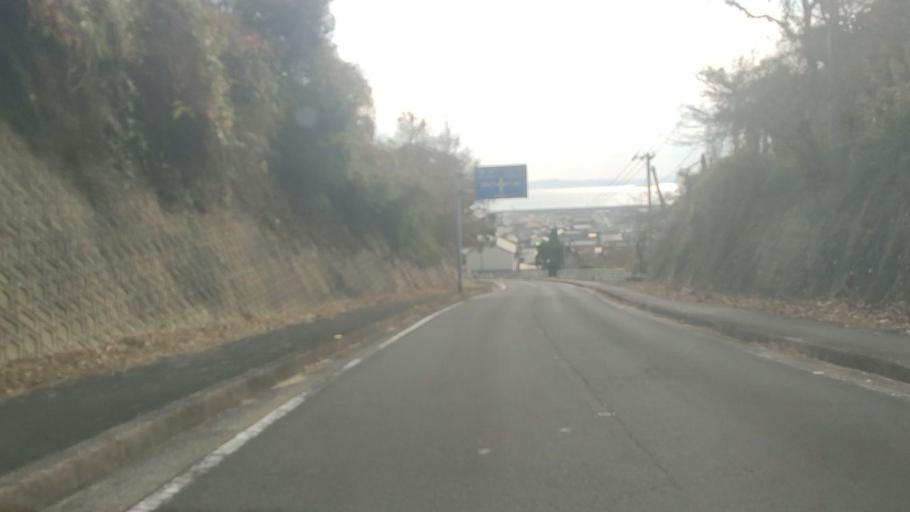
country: JP
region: Nagasaki
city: Shimabara
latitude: 32.6583
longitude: 130.2885
